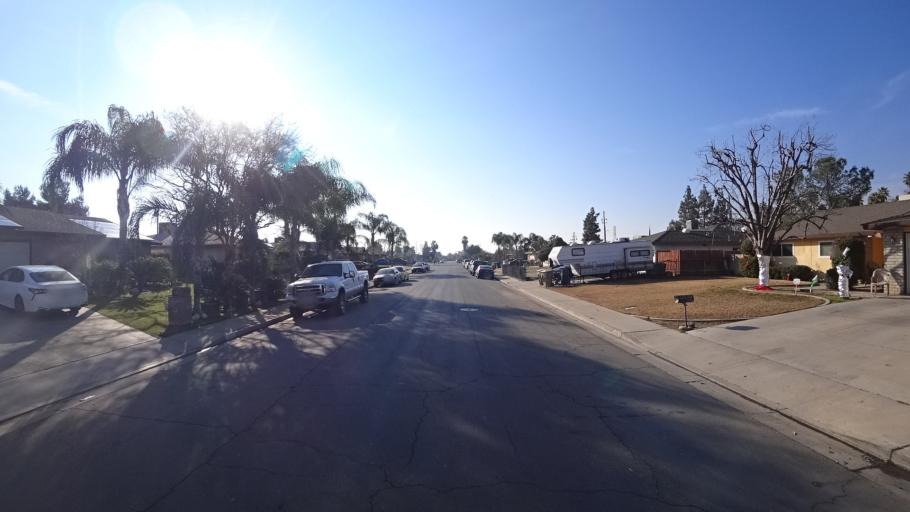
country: US
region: California
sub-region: Kern County
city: Greenfield
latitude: 35.3152
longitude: -119.0165
